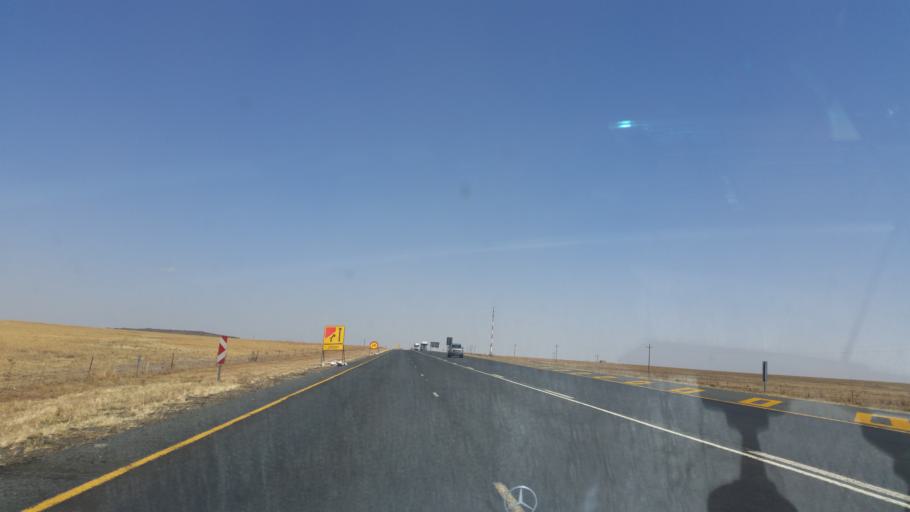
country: ZA
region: Orange Free State
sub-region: Lejweleputswa District Municipality
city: Brandfort
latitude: -28.8087
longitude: 26.6775
